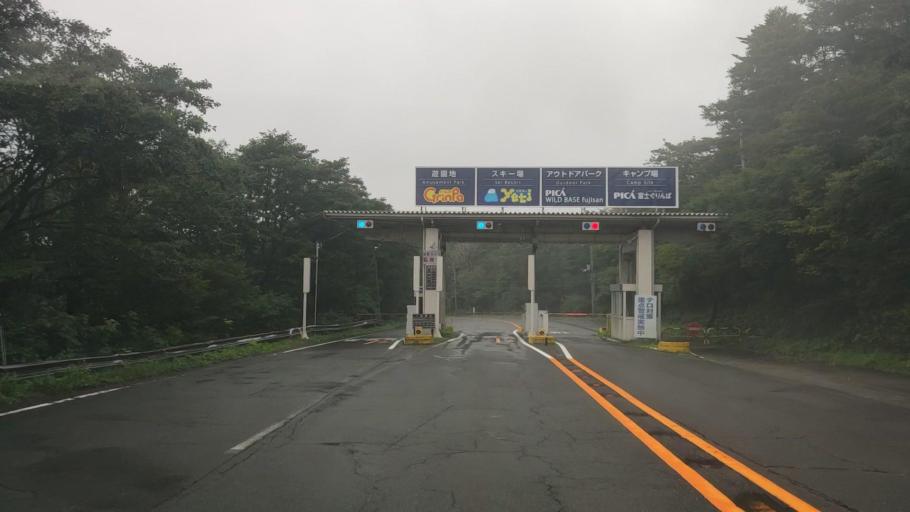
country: JP
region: Shizuoka
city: Fuji
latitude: 35.3014
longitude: 138.7704
